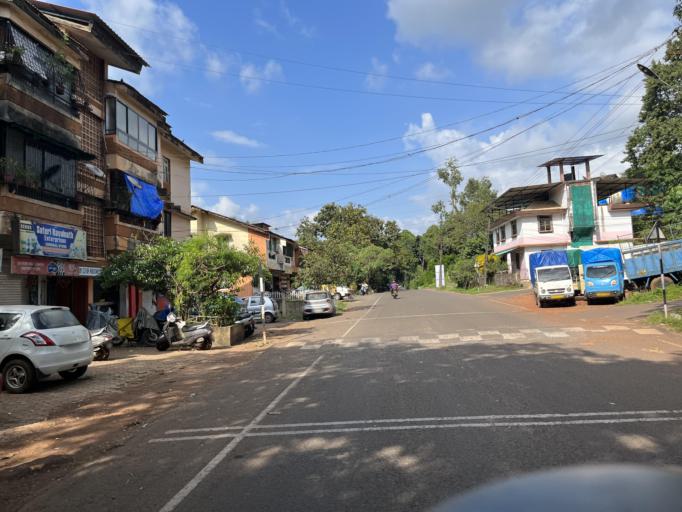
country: IN
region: Goa
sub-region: North Goa
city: Ponda
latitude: 15.4060
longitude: 74.0179
